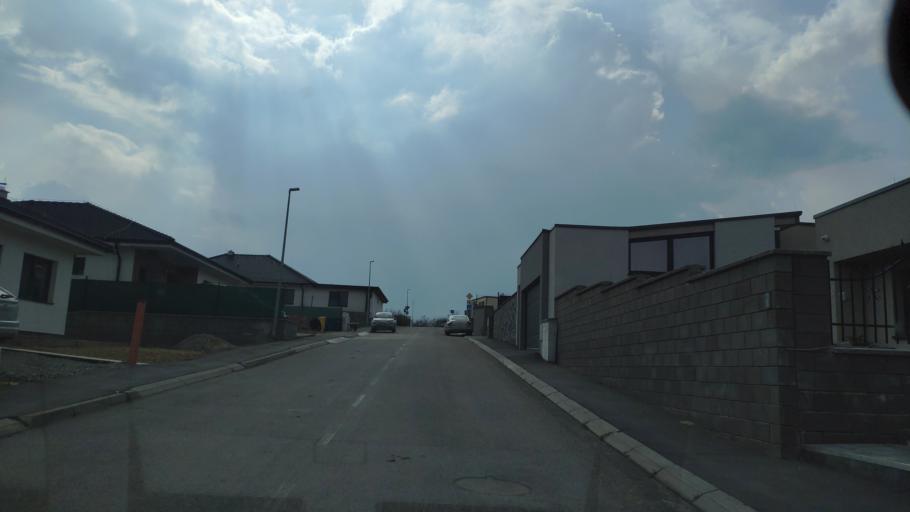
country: SK
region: Kosicky
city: Kosice
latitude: 48.6829
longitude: 21.3084
